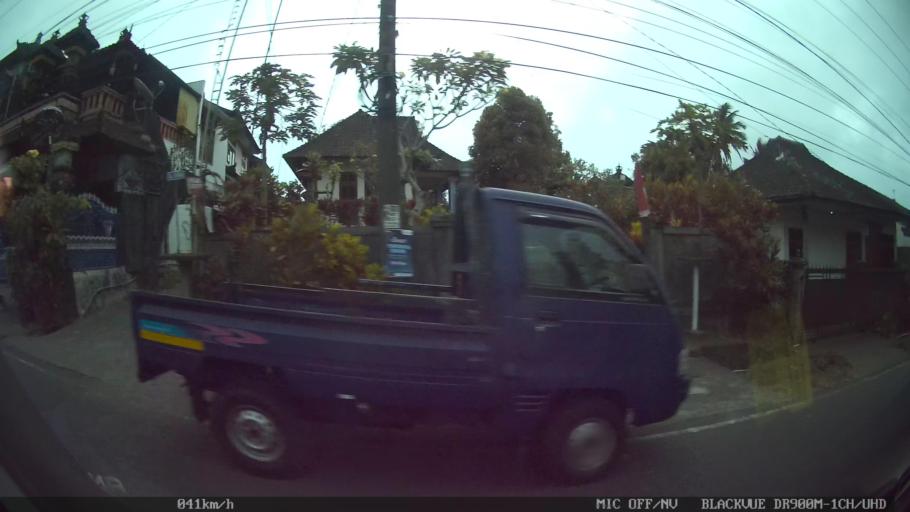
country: ID
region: Bali
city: Bantiran
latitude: -8.3265
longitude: 115.0296
